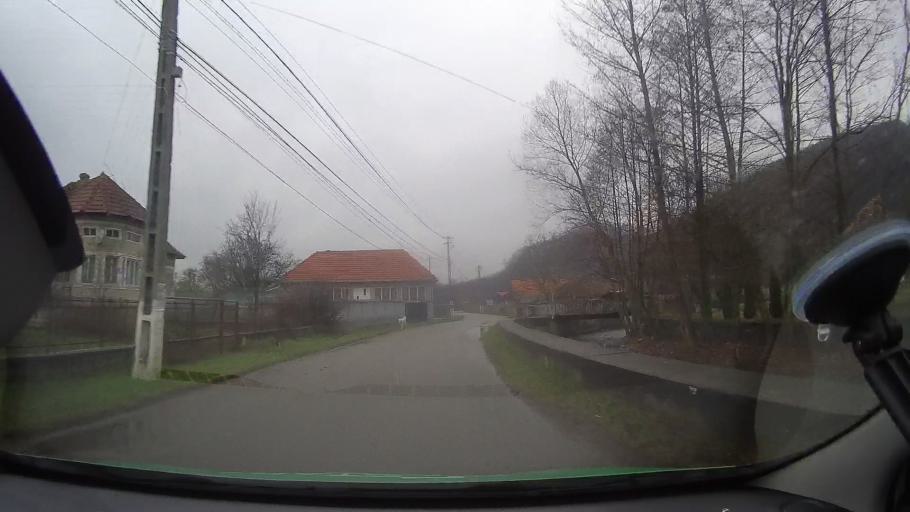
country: RO
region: Arad
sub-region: Comuna Halmagel
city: Halmagel
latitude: 46.2689
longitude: 22.6198
